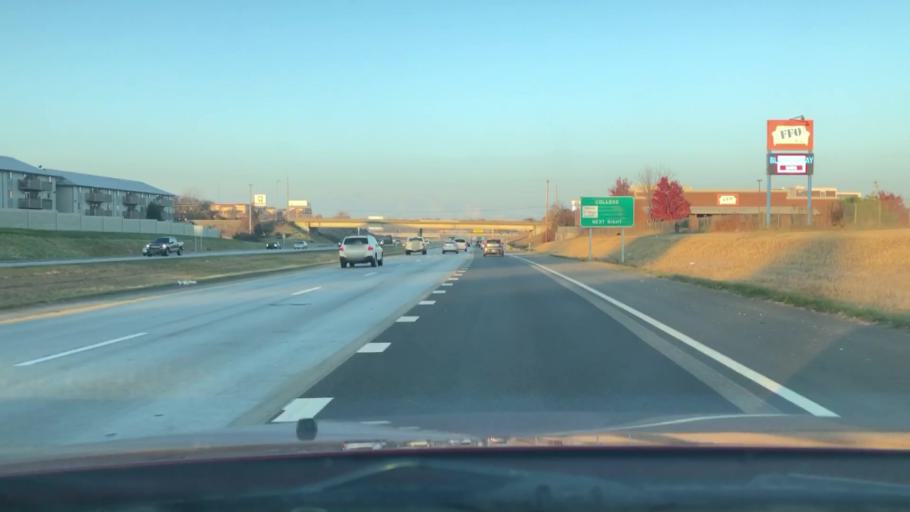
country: US
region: Missouri
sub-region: Greene County
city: Springfield
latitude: 37.1423
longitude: -93.2692
